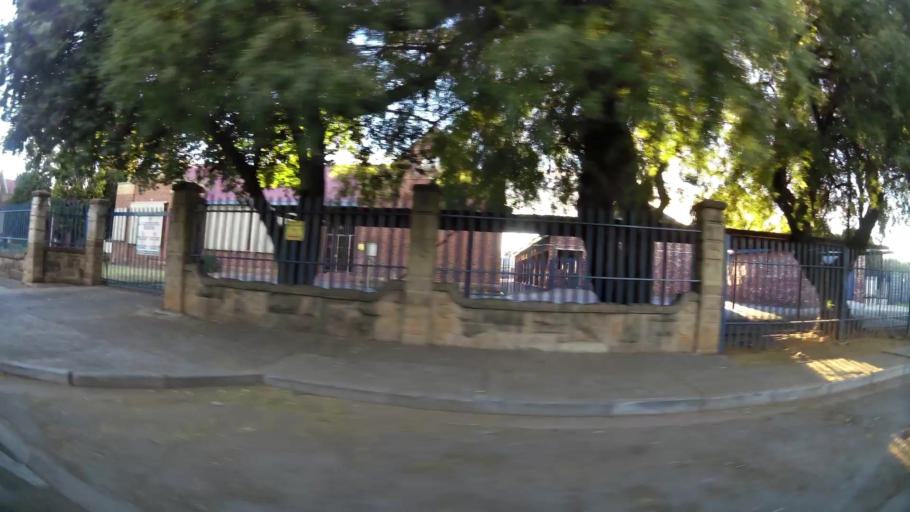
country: ZA
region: North-West
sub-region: Dr Kenneth Kaunda District Municipality
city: Potchefstroom
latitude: -26.7247
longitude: 27.0921
